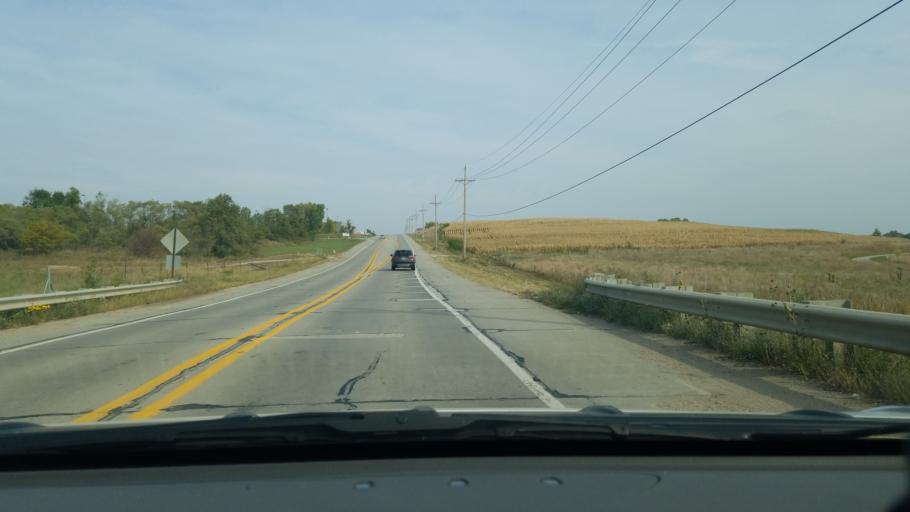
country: US
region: Nebraska
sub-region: Sarpy County
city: Chalco
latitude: 41.1495
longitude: -96.1195
